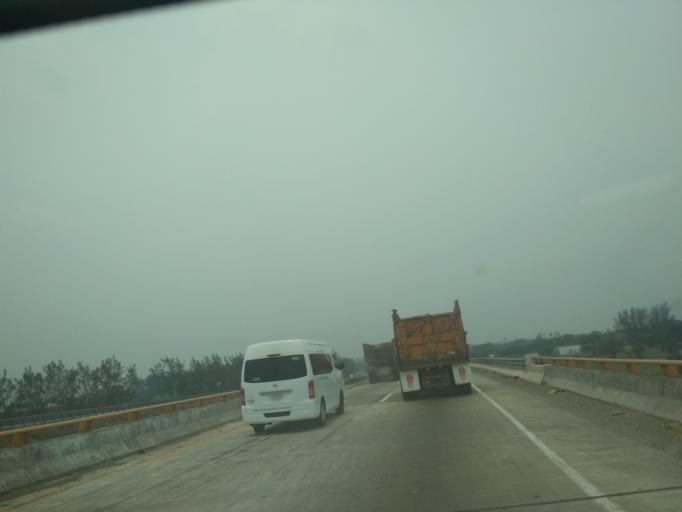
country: MX
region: Veracruz
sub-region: Veracruz
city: Oasis
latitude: 19.1847
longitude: -96.2465
